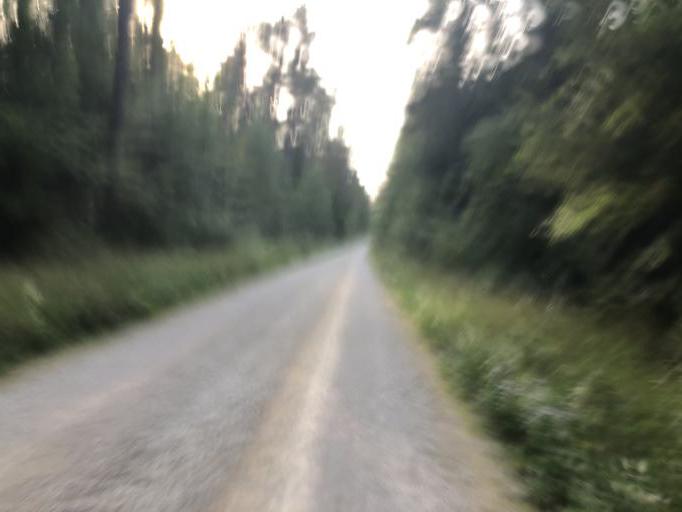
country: DE
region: Bavaria
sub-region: Regierungsbezirk Mittelfranken
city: Buckenhof
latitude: 49.5773
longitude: 11.0446
